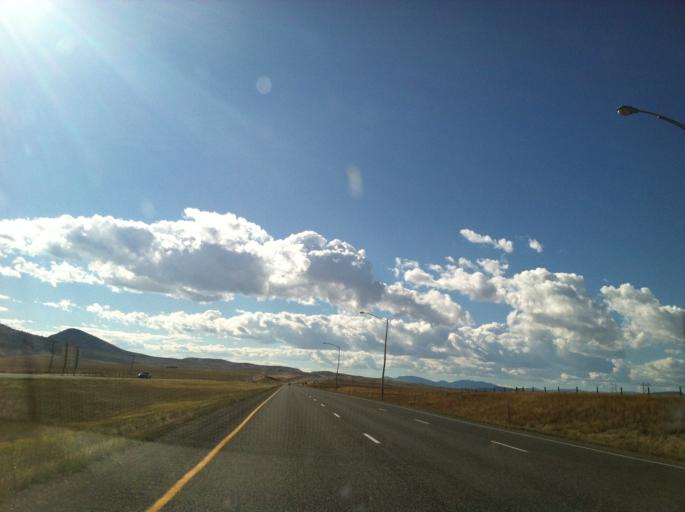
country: US
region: Montana
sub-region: Gallatin County
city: Three Forks
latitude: 45.9184
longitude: -111.6016
